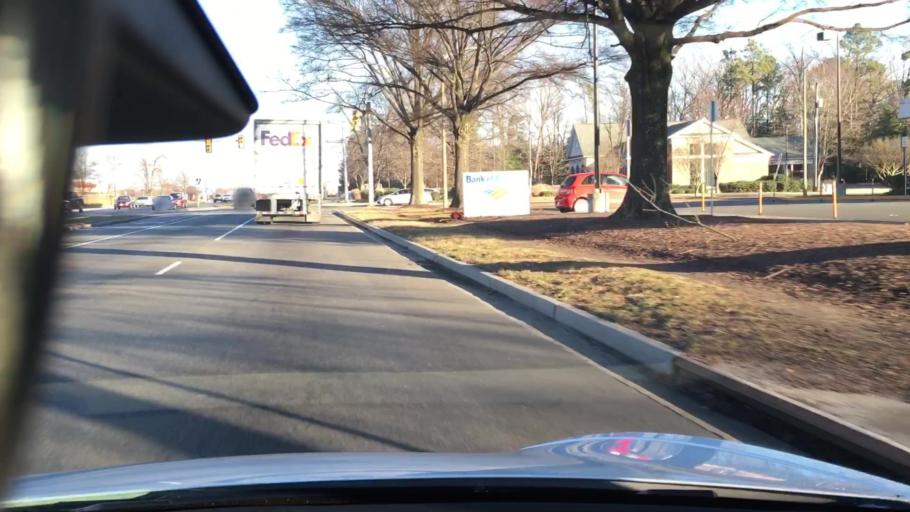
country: US
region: Virginia
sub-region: Henrico County
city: Montrose
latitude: 37.5209
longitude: -77.3514
